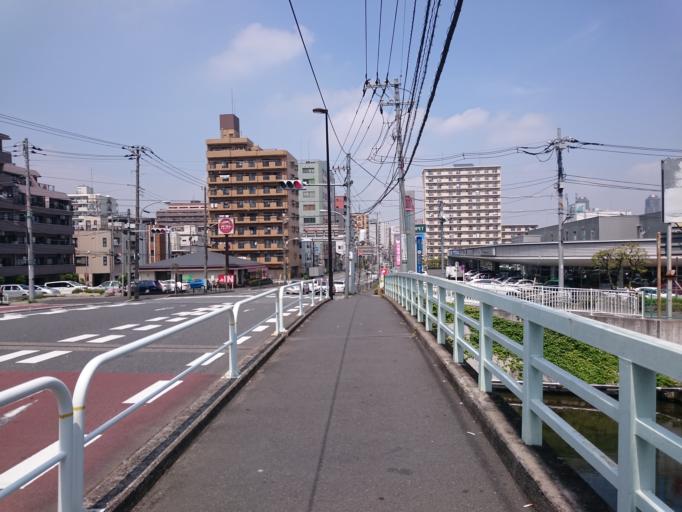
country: JP
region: Tokyo
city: Urayasu
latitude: 35.6762
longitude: 139.8160
